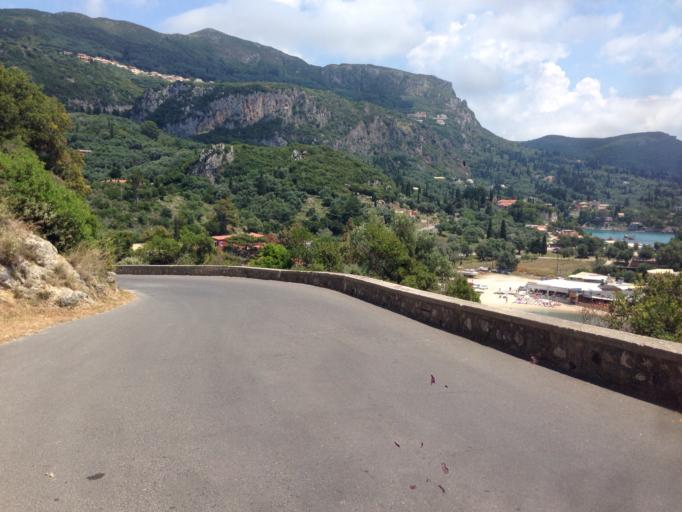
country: GR
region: Ionian Islands
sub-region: Nomos Kerkyras
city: Agios Georgis
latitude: 39.6708
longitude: 19.7022
